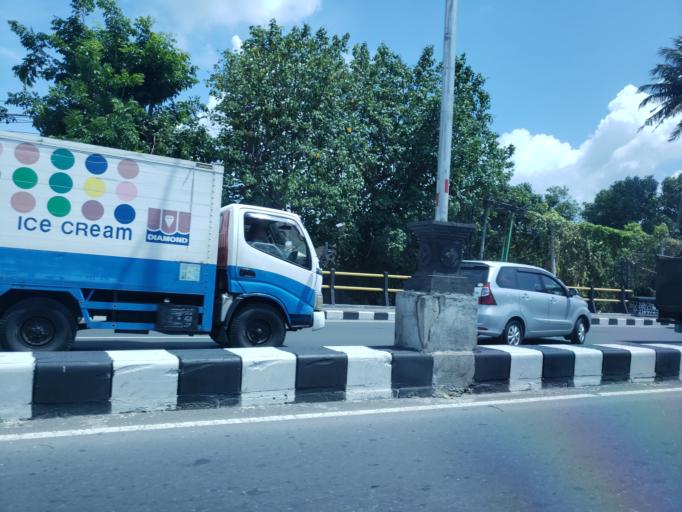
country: ID
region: Bali
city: Jabajero
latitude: -8.7282
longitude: 115.1796
